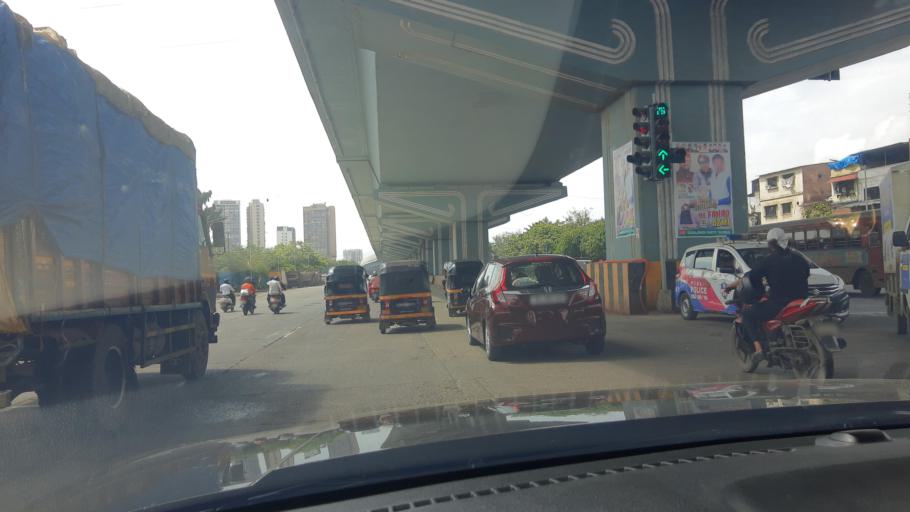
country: IN
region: Maharashtra
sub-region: Mumbai Suburban
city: Mumbai
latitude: 19.0592
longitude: 72.9239
